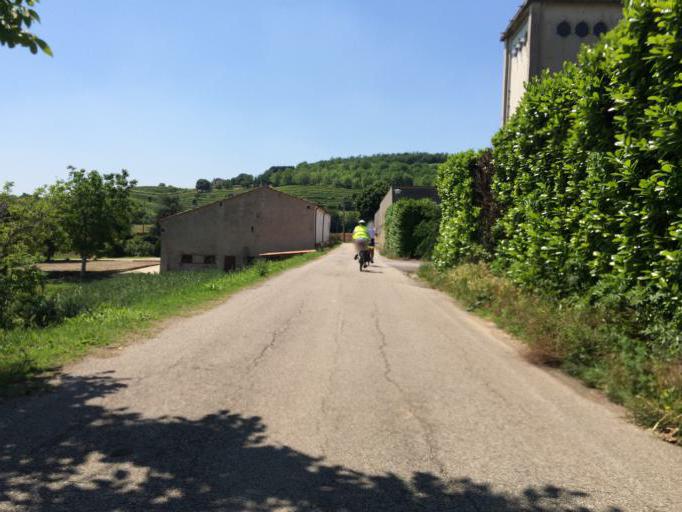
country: IT
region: Veneto
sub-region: Provincia di Vicenza
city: Villaga
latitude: 45.4027
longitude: 11.5362
